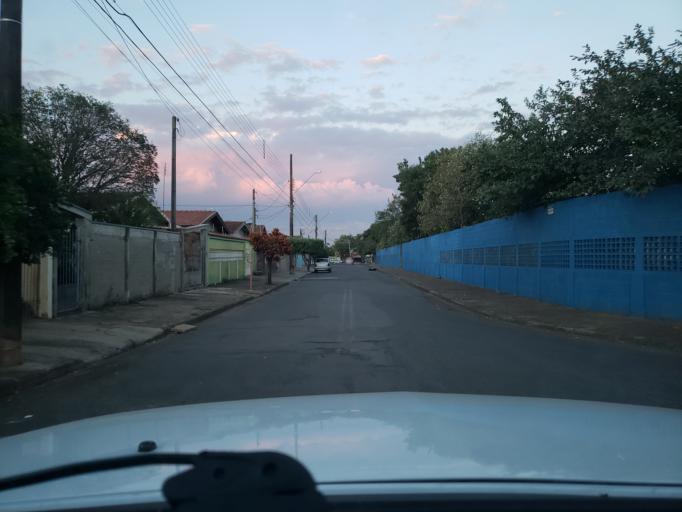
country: BR
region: Sao Paulo
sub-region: Moji-Guacu
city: Mogi-Gaucu
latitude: -22.3428
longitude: -46.9431
